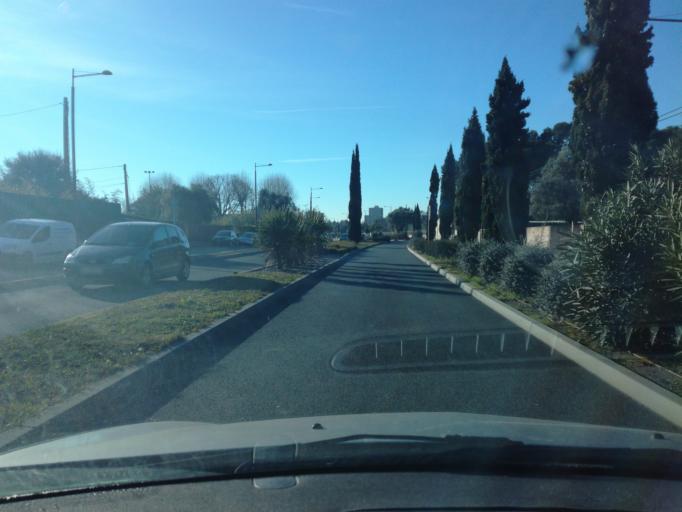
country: FR
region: Provence-Alpes-Cote d'Azur
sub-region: Departement des Alpes-Maritimes
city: Vallauris
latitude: 43.5834
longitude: 7.0898
